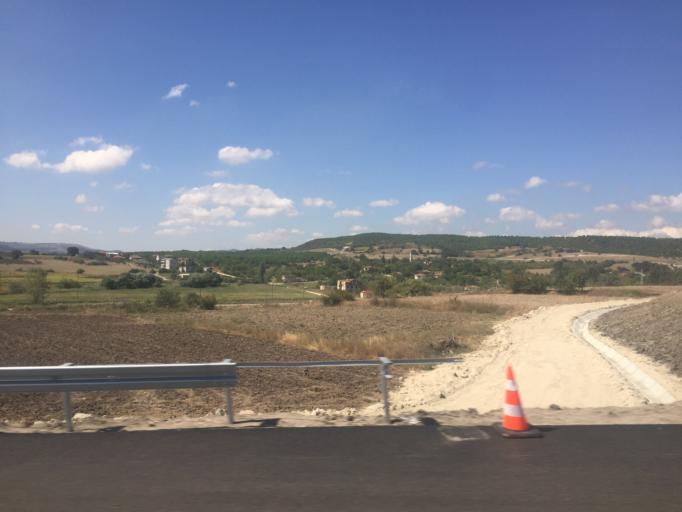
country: TR
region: Balikesir
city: Susurluk
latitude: 39.9592
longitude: 28.1661
